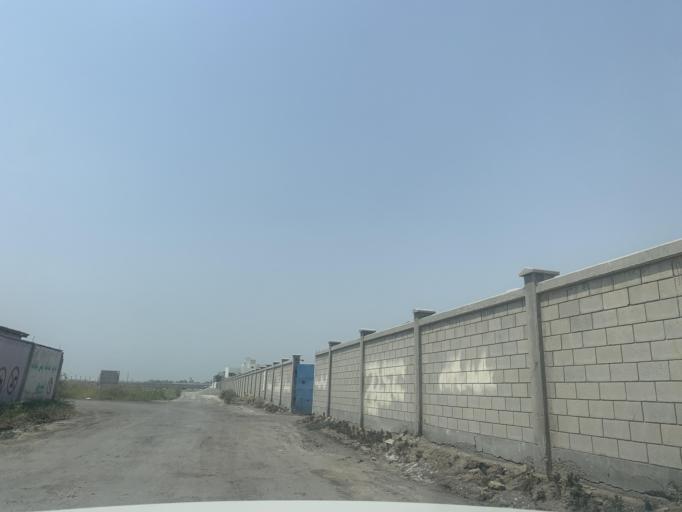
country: BH
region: Central Governorate
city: Madinat Hamad
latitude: 26.1229
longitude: 50.4644
